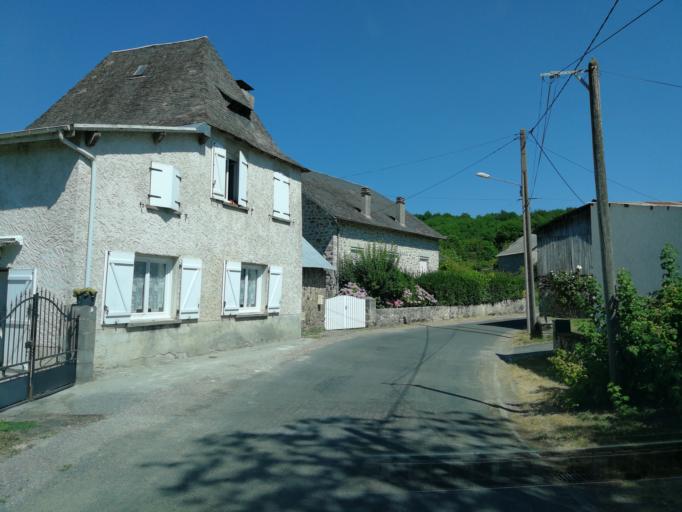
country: FR
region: Limousin
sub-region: Departement de la Correze
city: Sainte-Fereole
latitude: 45.2404
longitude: 1.5929
